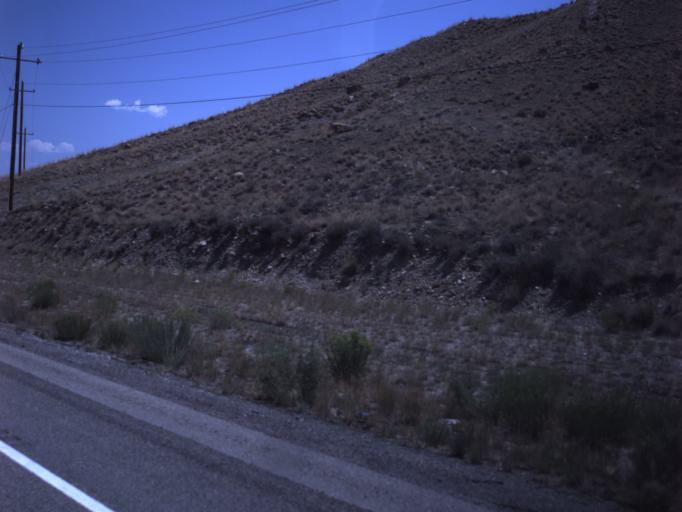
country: US
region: Utah
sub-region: Emery County
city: Ferron
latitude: 39.1519
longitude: -111.0864
